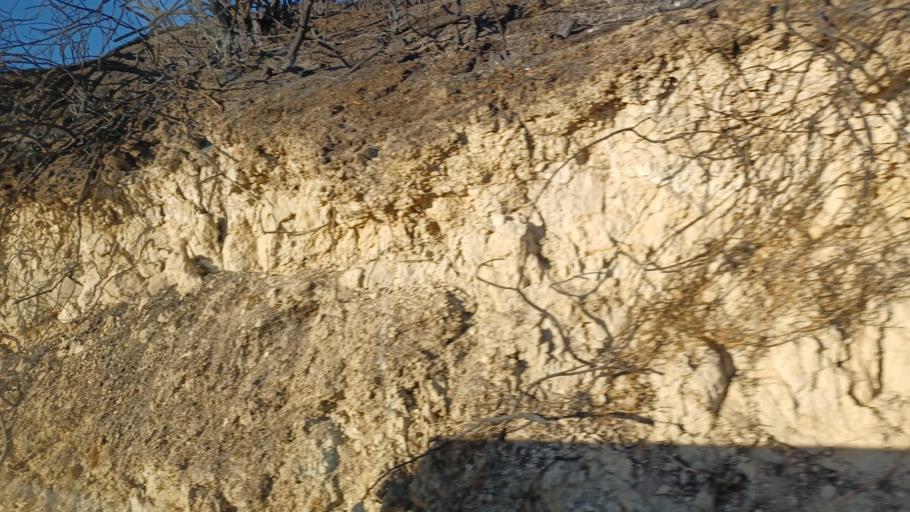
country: CY
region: Pafos
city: Polis
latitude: 34.9749
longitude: 32.4584
